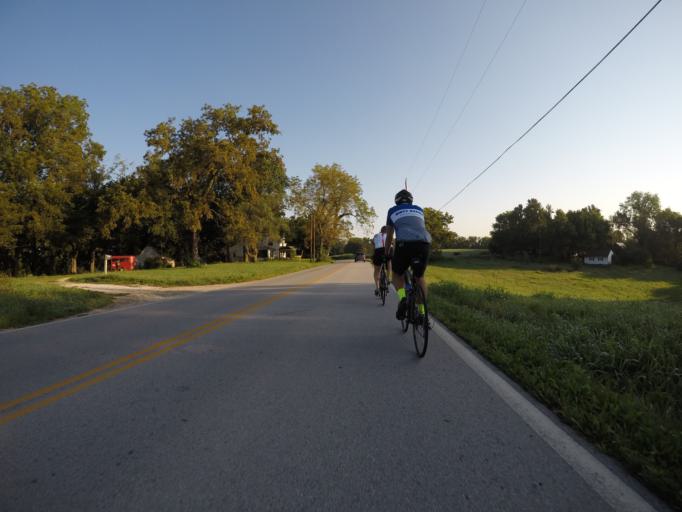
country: US
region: Kansas
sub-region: Leavenworth County
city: Lansing
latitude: 39.2441
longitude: -94.8723
